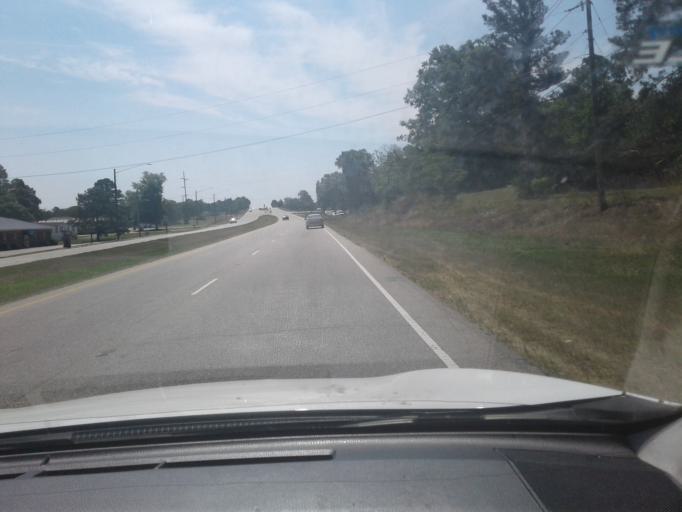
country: US
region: North Carolina
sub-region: Harnett County
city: Erwin
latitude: 35.3328
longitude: -78.6698
